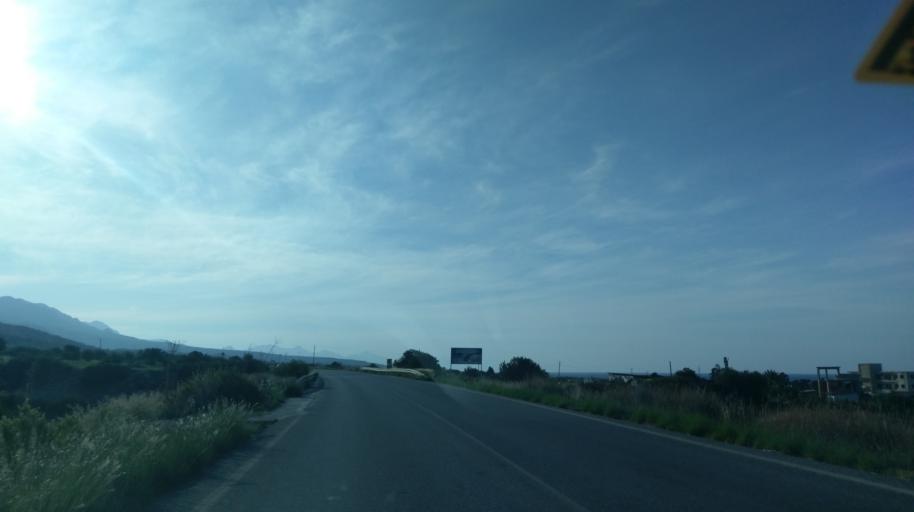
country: CY
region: Ammochostos
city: Lefkonoiko
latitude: 35.3625
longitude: 33.6723
